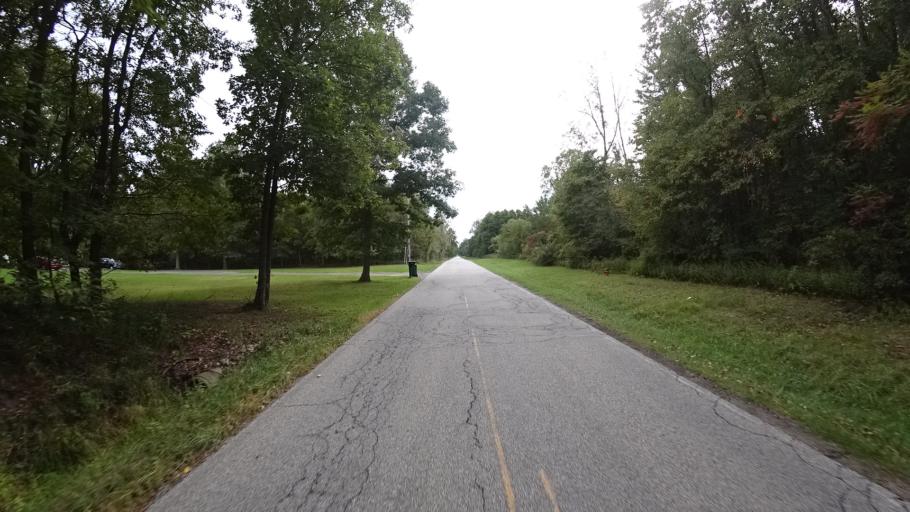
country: US
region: Indiana
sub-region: LaPorte County
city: Long Beach
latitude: 41.7365
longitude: -86.8161
